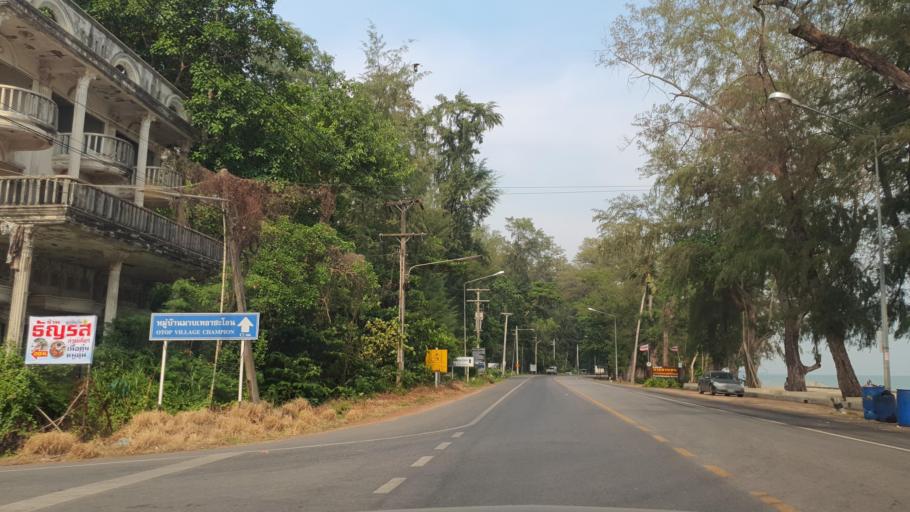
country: TH
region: Rayong
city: Rayong
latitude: 12.6316
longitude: 101.4515
